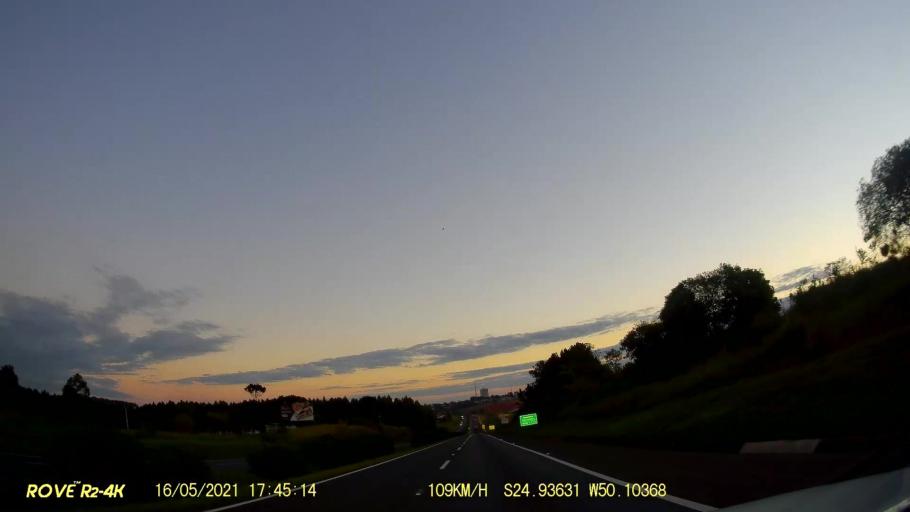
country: BR
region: Parana
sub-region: Carambei
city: Carambei
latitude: -24.9366
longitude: -50.1039
